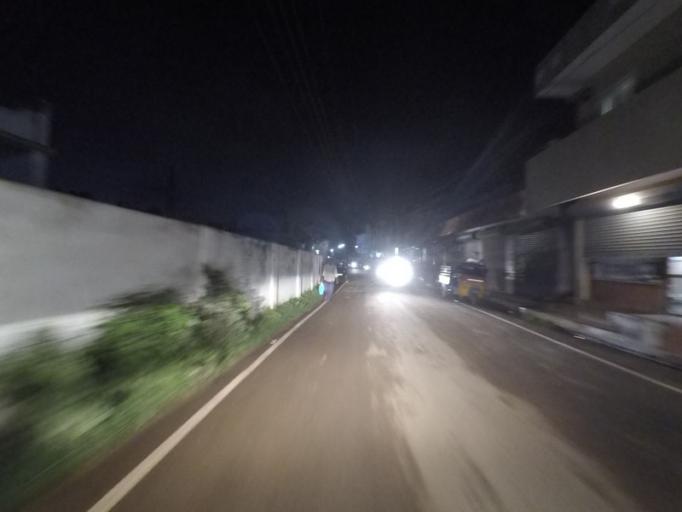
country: IN
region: Tamil Nadu
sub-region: Nilgiri
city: Kotagiri
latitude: 11.4269
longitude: 76.8666
